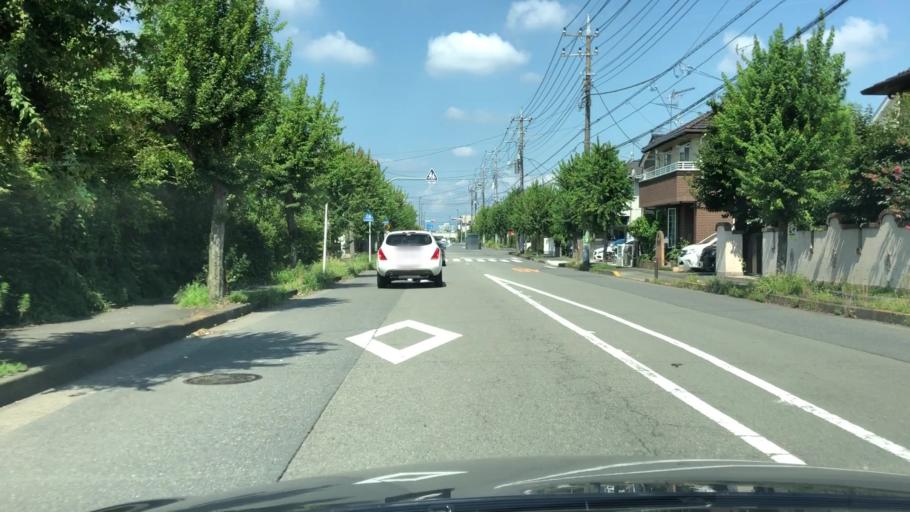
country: JP
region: Tokyo
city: Hino
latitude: 35.6817
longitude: 139.3994
